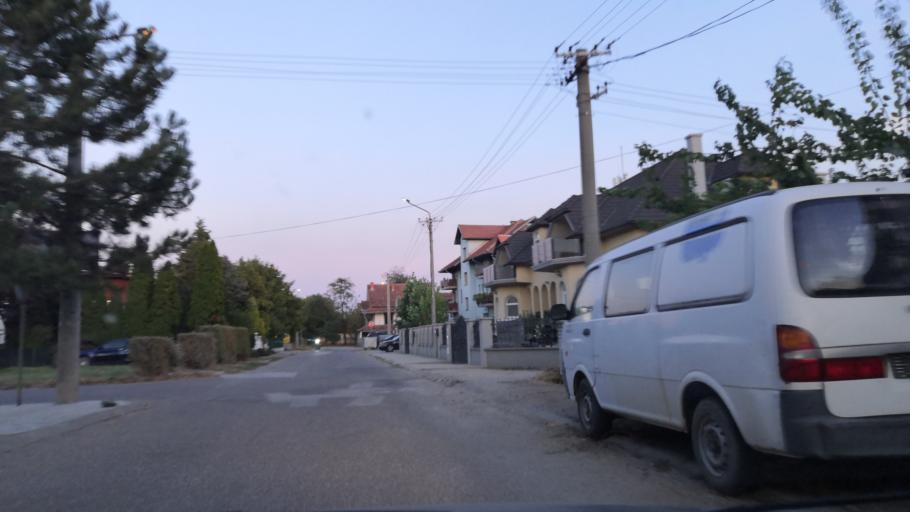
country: RS
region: Central Serbia
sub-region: Borski Okrug
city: Negotin
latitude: 44.2394
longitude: 22.5293
